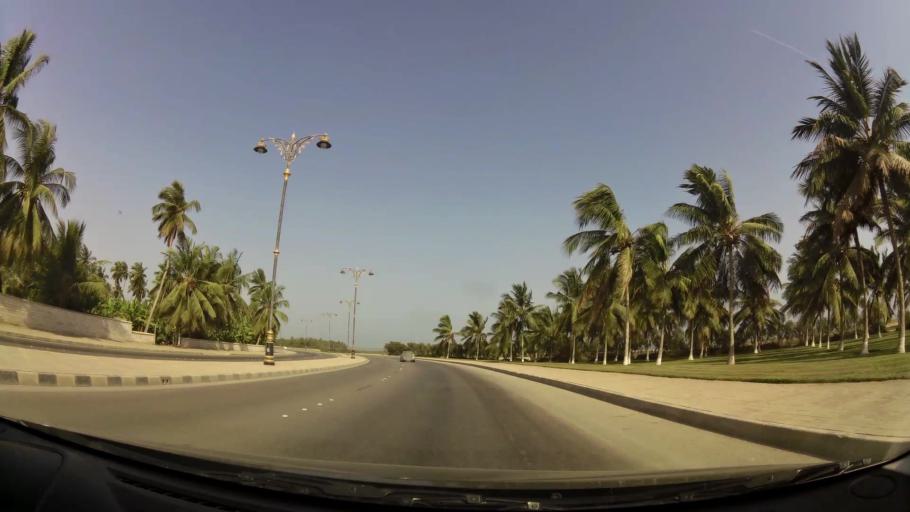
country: OM
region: Zufar
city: Salalah
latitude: 16.9989
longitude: 54.0709
